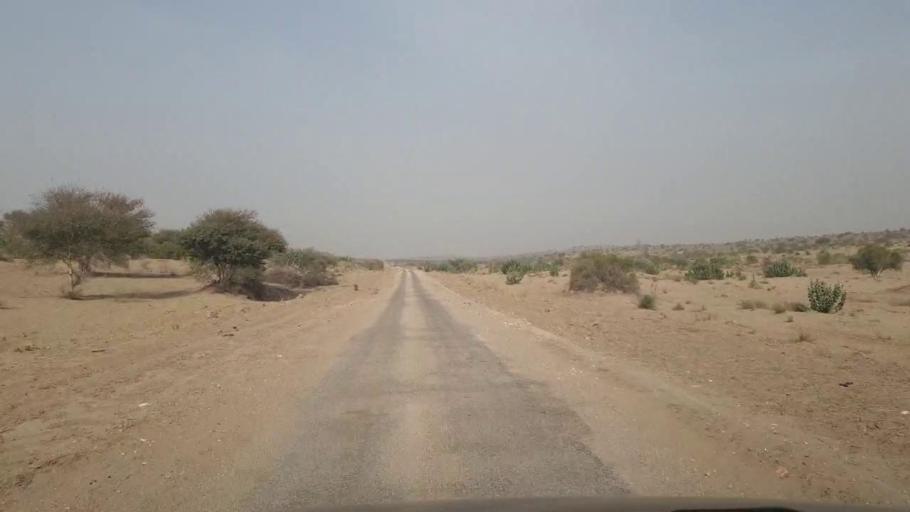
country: PK
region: Sindh
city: Chor
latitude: 25.6256
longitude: 69.9405
